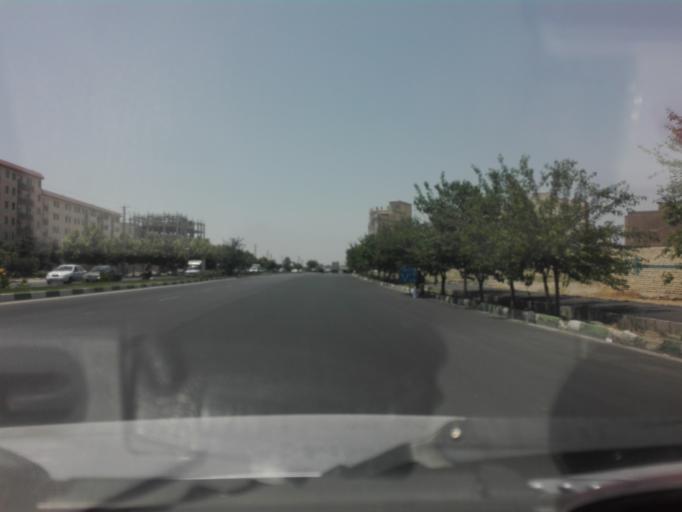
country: IR
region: Tehran
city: Malard
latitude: 35.7122
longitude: 50.9760
